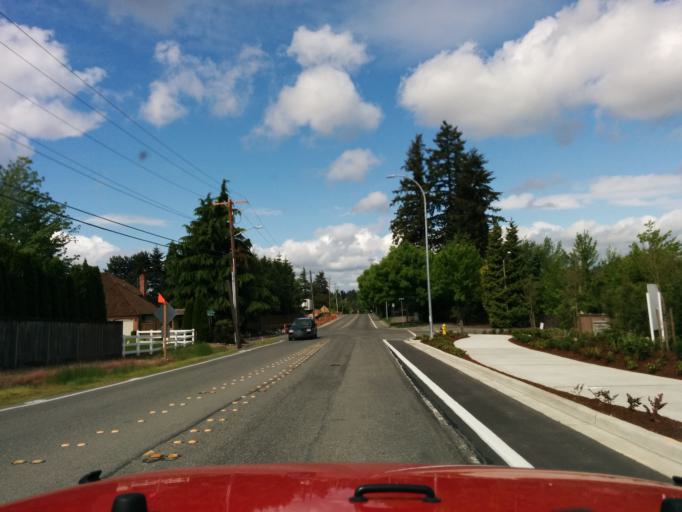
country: US
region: Washington
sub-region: King County
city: Redmond
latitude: 47.7039
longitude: -122.1261
